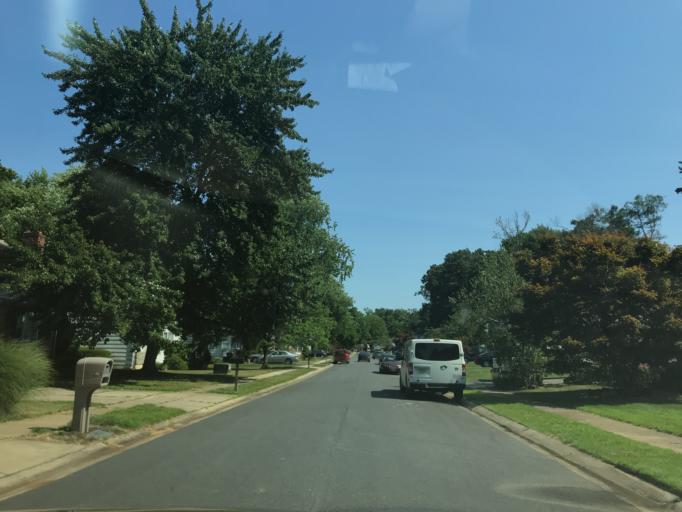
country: US
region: Delaware
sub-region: New Castle County
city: Claymont
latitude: 39.8331
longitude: -75.5174
